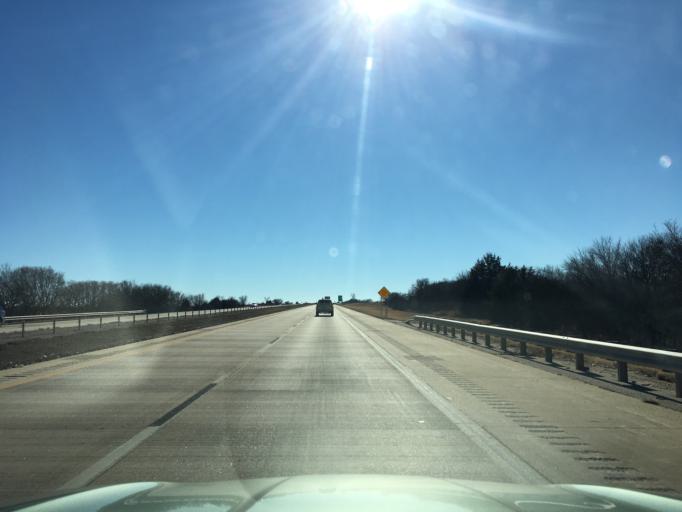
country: US
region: Oklahoma
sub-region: Noble County
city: Perry
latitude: 36.4386
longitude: -97.3271
